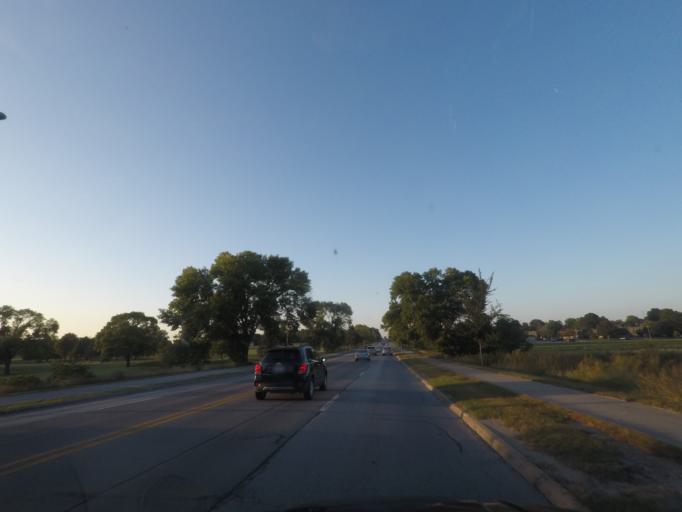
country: US
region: Iowa
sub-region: Story County
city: Ames
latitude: 42.0373
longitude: -93.6448
